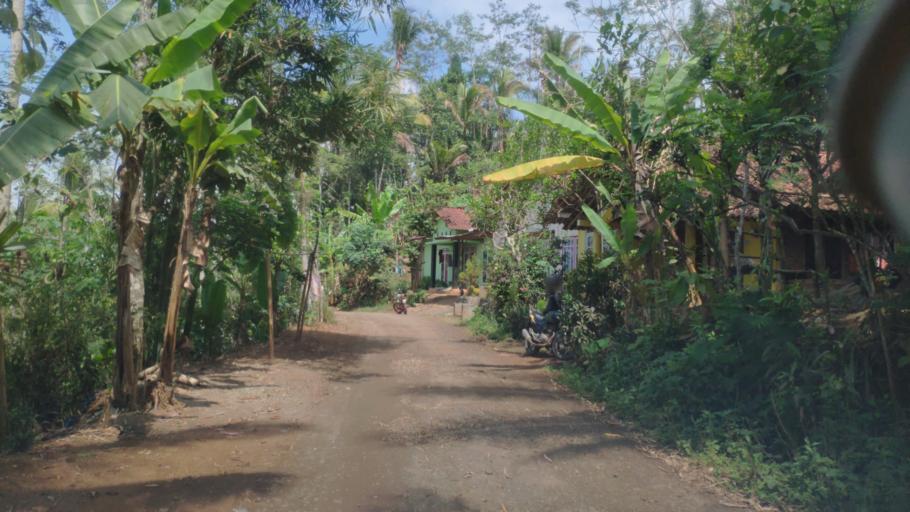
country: ID
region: Central Java
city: Purbalingga
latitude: -7.3451
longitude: 109.6151
